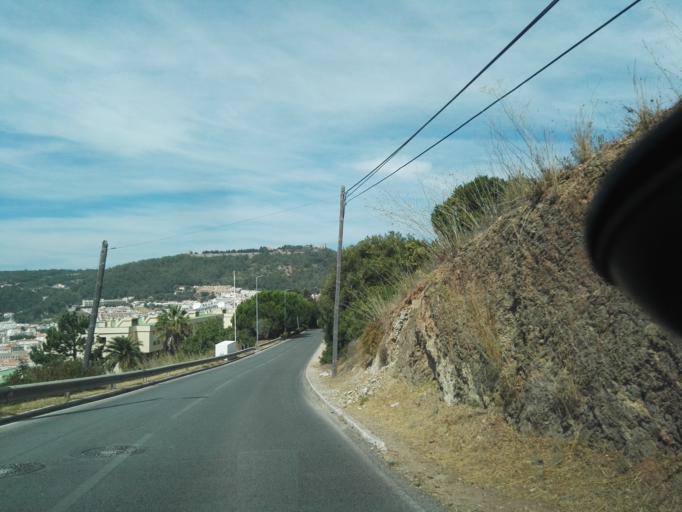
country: PT
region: Setubal
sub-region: Sesimbra
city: Sesimbra
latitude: 38.4432
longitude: -9.0925
